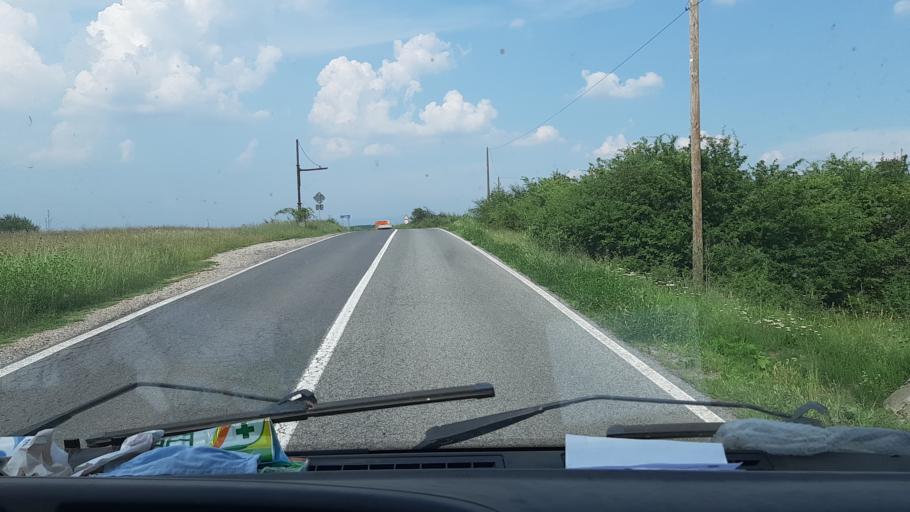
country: RO
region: Caras-Severin
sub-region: Comuna Farliug
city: Farliug
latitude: 45.5239
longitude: 21.8766
